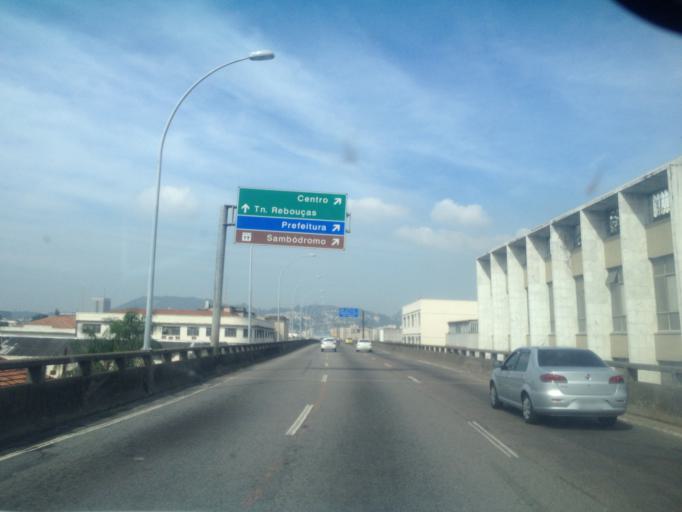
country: BR
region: Rio de Janeiro
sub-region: Rio De Janeiro
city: Rio de Janeiro
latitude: -22.8987
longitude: -43.2186
